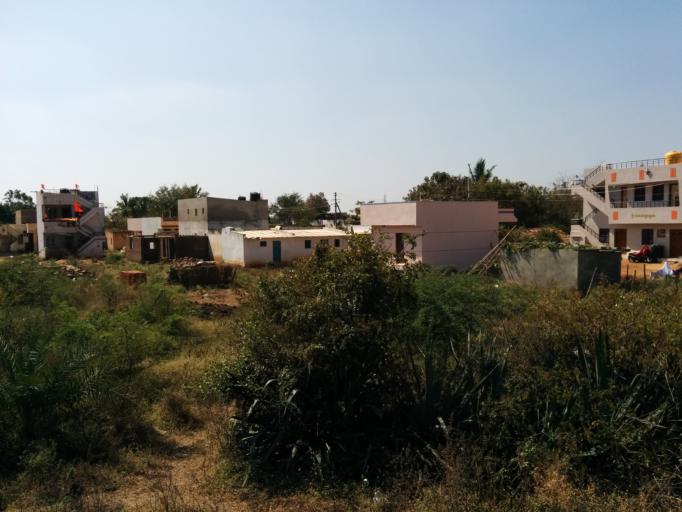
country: IN
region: Karnataka
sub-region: Dharwad
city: Hubli
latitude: 15.3907
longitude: 75.1155
